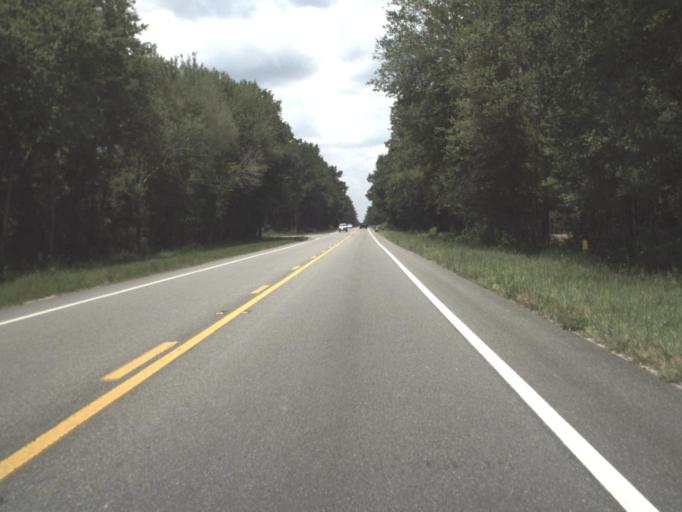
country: US
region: Florida
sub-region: Columbia County
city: Five Points
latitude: 30.2563
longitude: -82.6824
